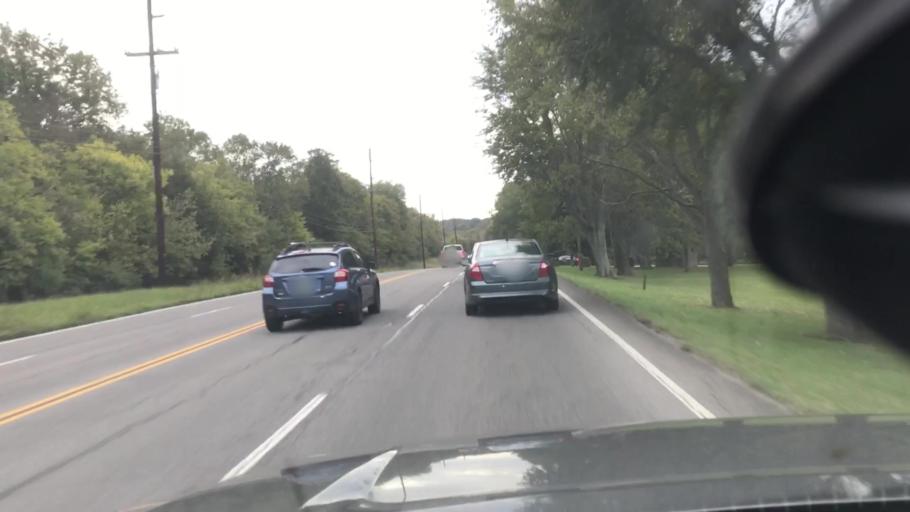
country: US
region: Tennessee
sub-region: Davidson County
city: Belle Meade
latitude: 36.0612
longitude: -86.9123
